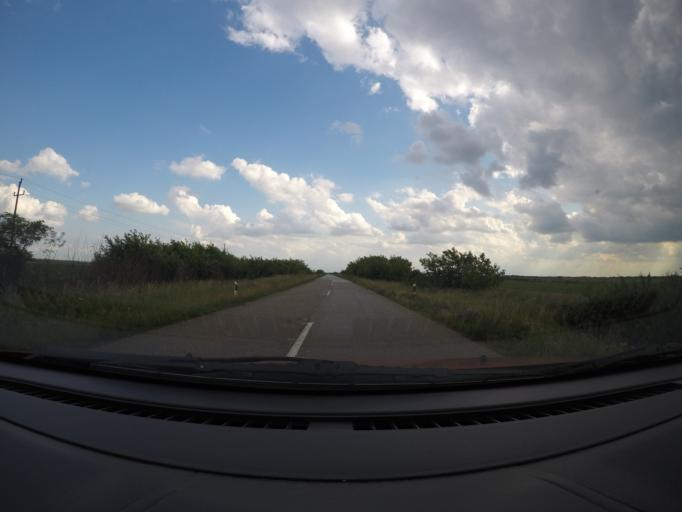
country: RS
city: Tomasevac
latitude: 45.2485
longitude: 20.6292
